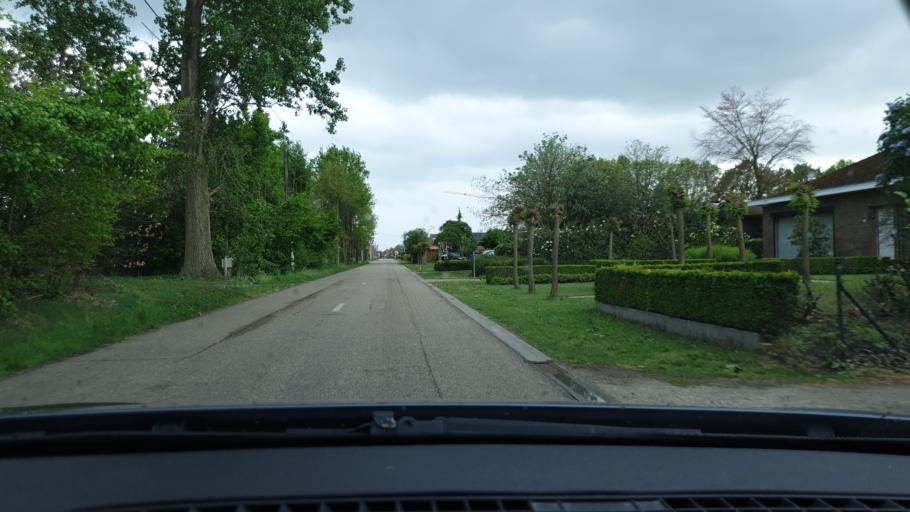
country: BE
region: Flanders
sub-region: Provincie Antwerpen
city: Geel
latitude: 51.1822
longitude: 4.9959
